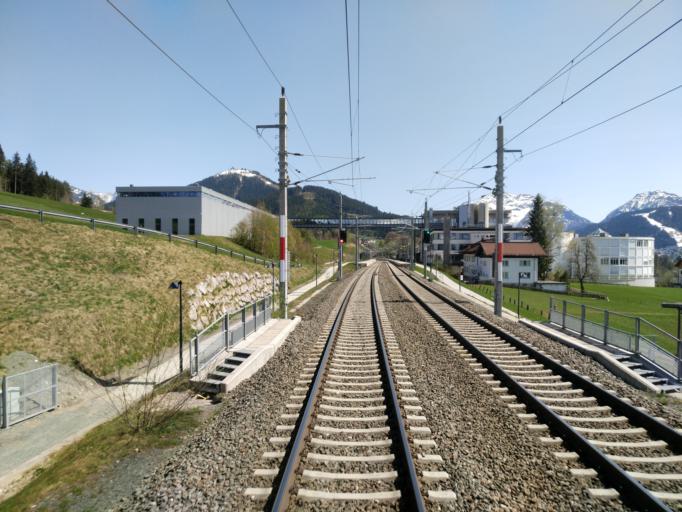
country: AT
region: Tyrol
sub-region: Politischer Bezirk Kitzbuhel
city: Fieberbrunn
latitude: 47.4921
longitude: 12.5264
